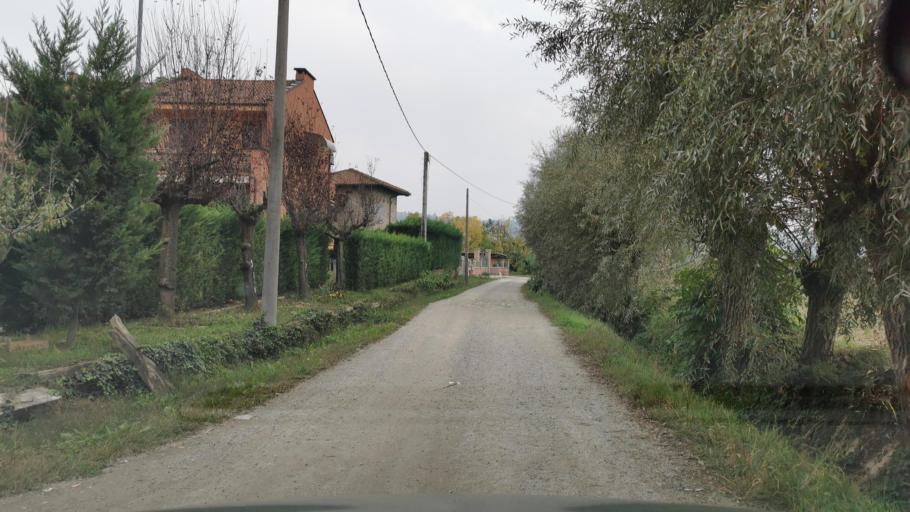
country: IT
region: Piedmont
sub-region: Provincia di Cuneo
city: Cinzano
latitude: 44.6926
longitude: 7.9120
